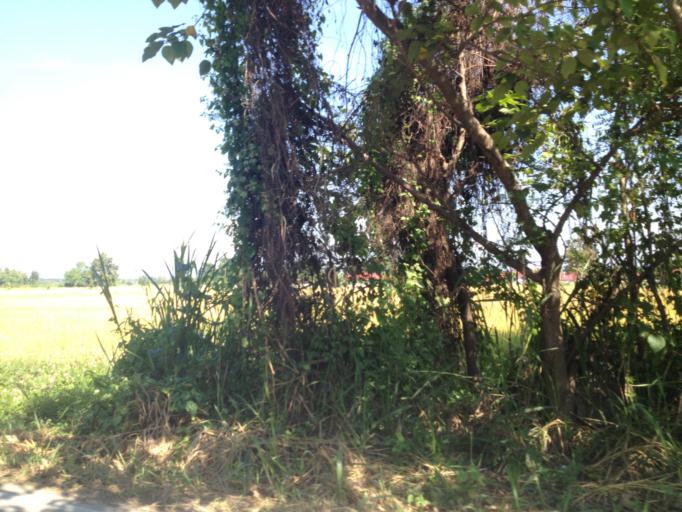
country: TH
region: Chiang Mai
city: Hang Dong
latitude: 18.7081
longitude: 98.9665
